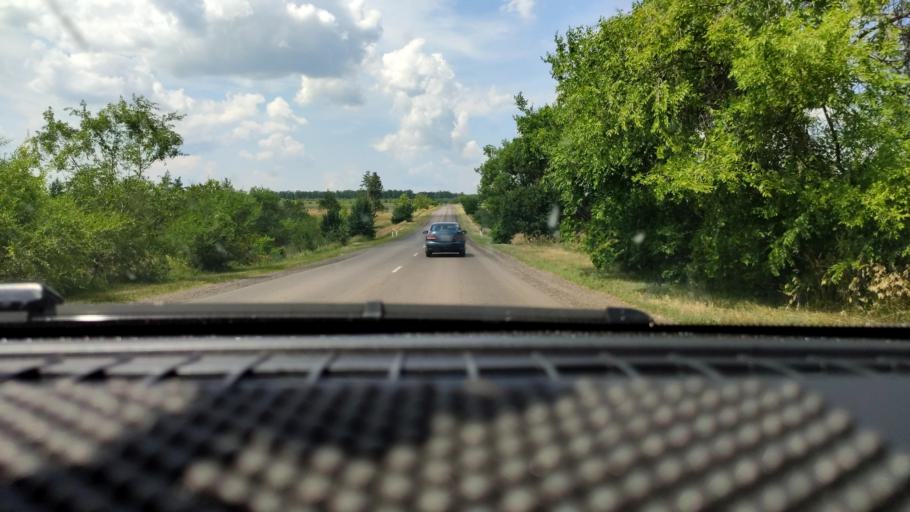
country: RU
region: Voronezj
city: Podkletnoye
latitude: 51.6312
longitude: 39.5189
